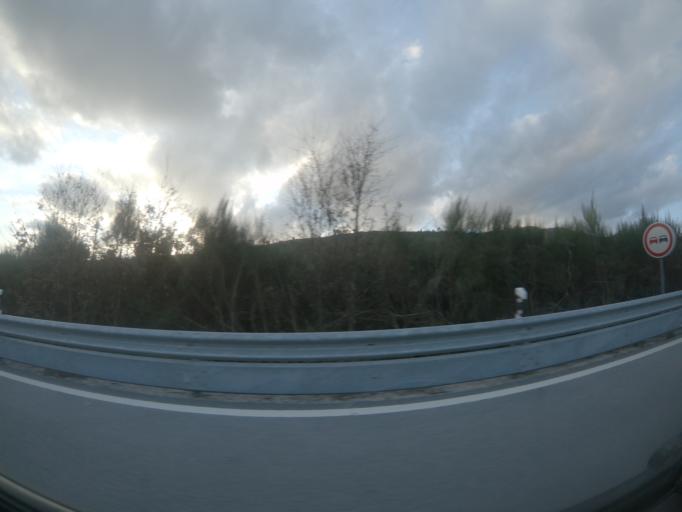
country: PT
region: Braganca
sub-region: Carrazeda de Ansiaes
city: Carrazeda de Anciaes
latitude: 41.2084
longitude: -7.3354
